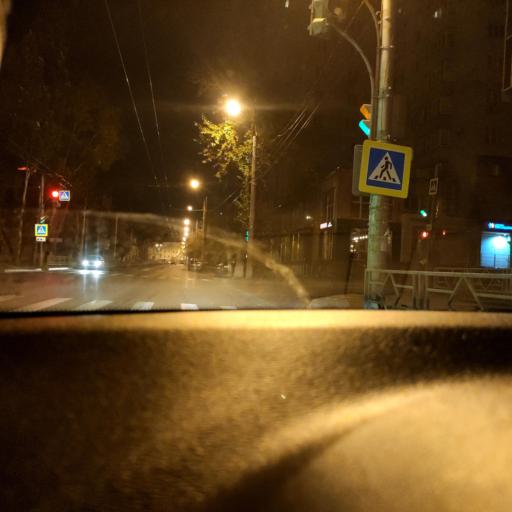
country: RU
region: Samara
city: Samara
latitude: 53.2007
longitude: 50.1414
